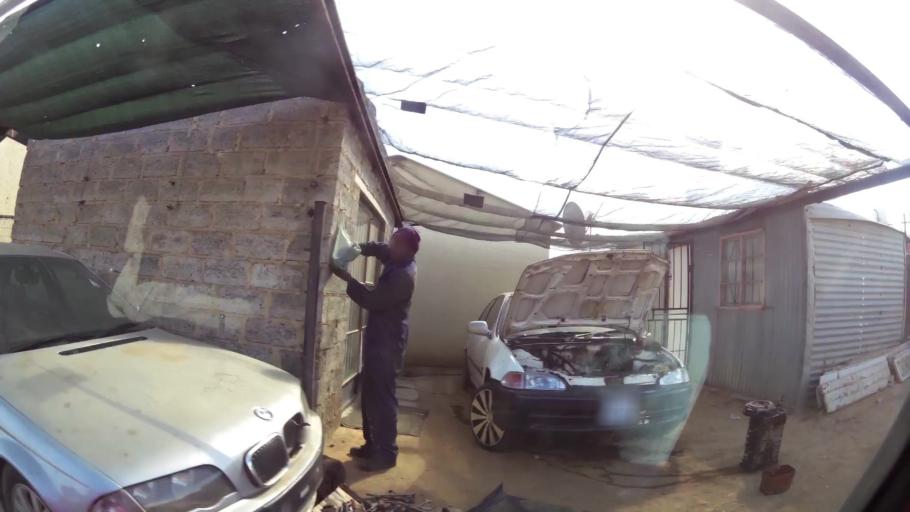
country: ZA
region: Gauteng
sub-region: City of Johannesburg Metropolitan Municipality
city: Midrand
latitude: -26.0297
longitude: 28.1685
